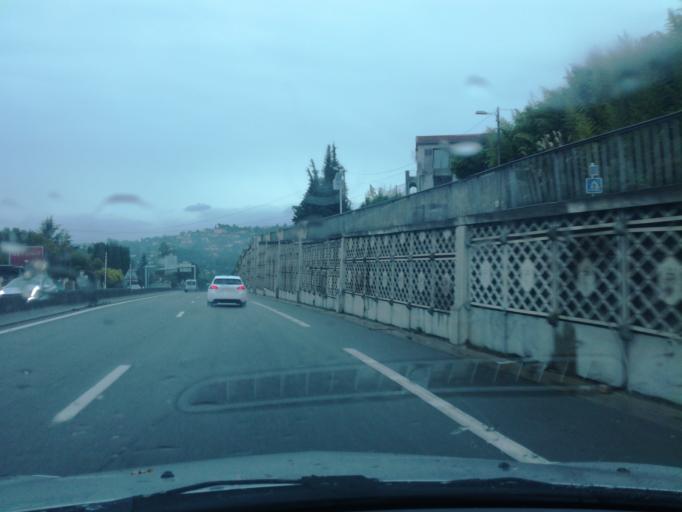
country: FR
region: Provence-Alpes-Cote d'Azur
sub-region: Departement des Alpes-Maritimes
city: Mougins
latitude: 43.5870
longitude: 7.0049
